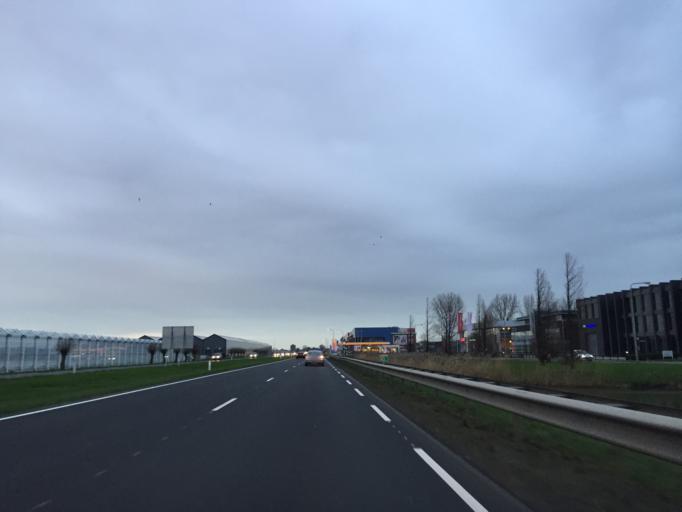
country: NL
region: South Holland
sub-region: Gemeente Westland
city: Kwintsheul
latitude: 52.0119
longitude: 4.2837
